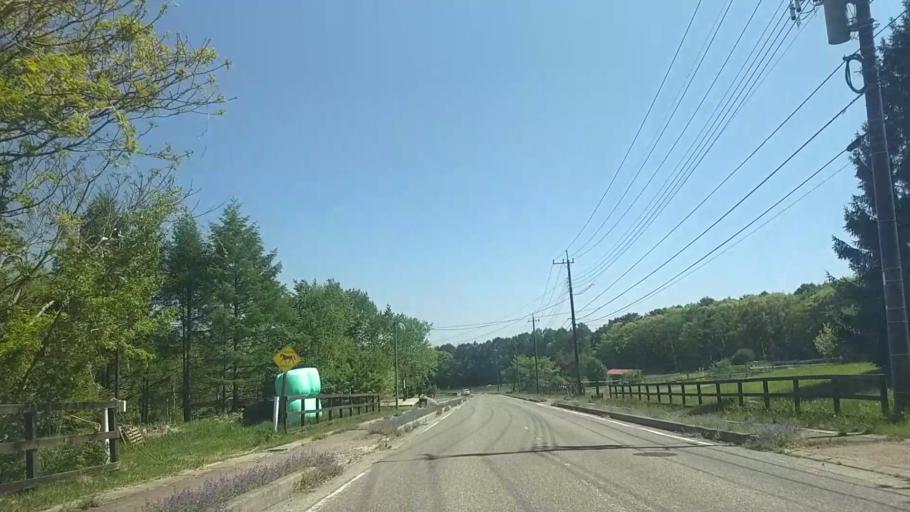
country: JP
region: Yamanashi
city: Nirasaki
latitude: 35.9096
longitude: 138.4322
